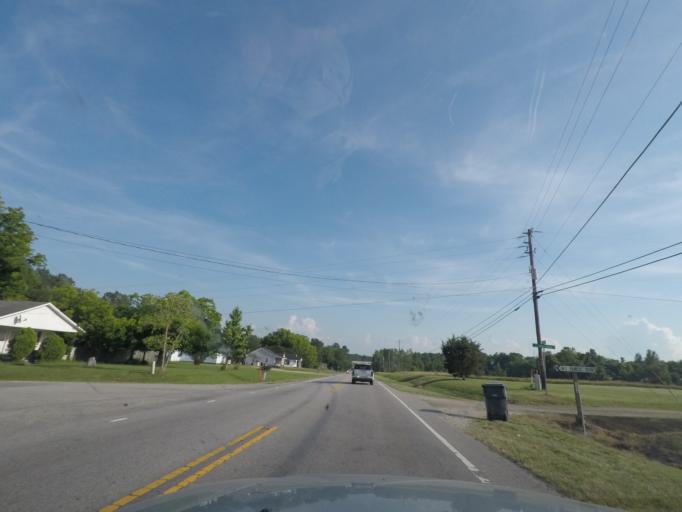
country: US
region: North Carolina
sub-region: Granville County
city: Oxford
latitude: 36.2787
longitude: -78.6072
